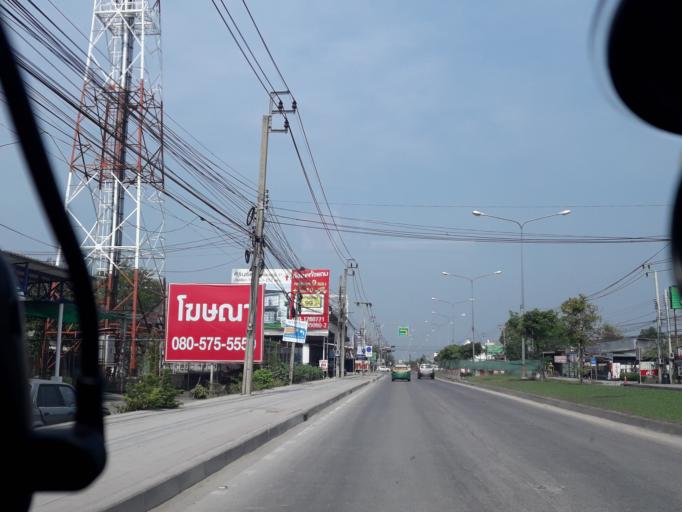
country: TH
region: Bangkok
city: Khlong Sam Wa
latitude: 13.8398
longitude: 100.7203
